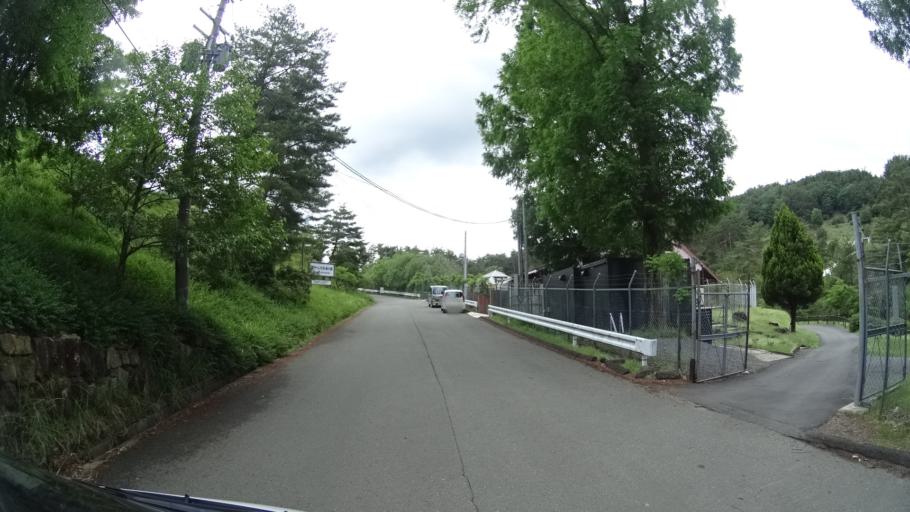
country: JP
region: Hyogo
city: Sasayama
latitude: 35.0300
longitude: 135.3987
